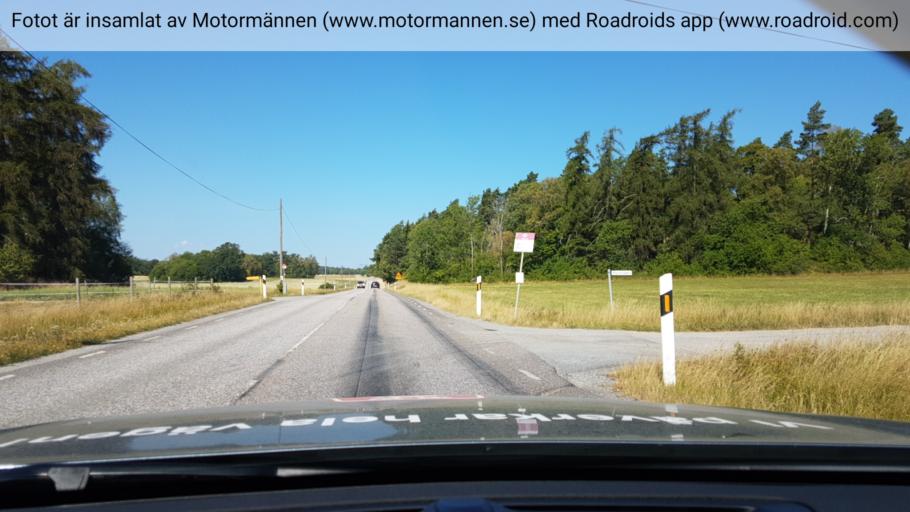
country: SE
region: Stockholm
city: Stenhamra
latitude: 59.2933
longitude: 17.6839
